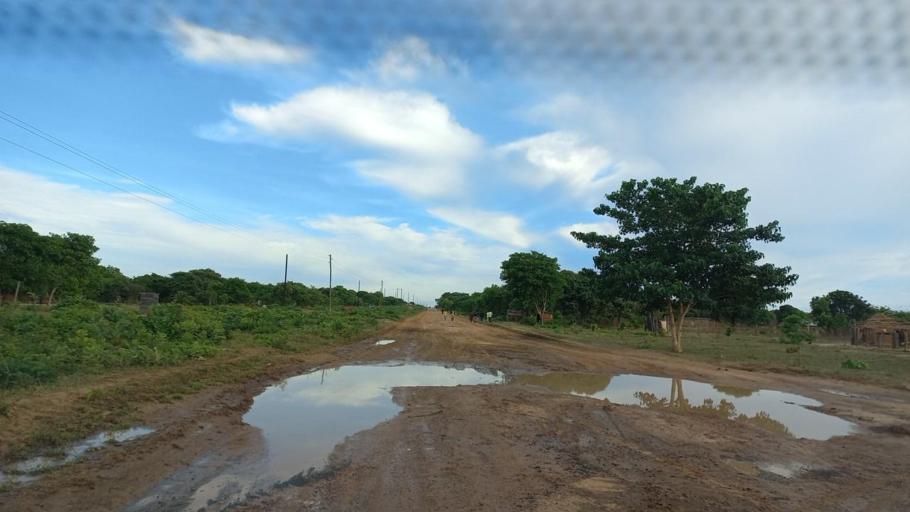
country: ZM
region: North-Western
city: Kabompo
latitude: -13.4243
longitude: 24.3248
